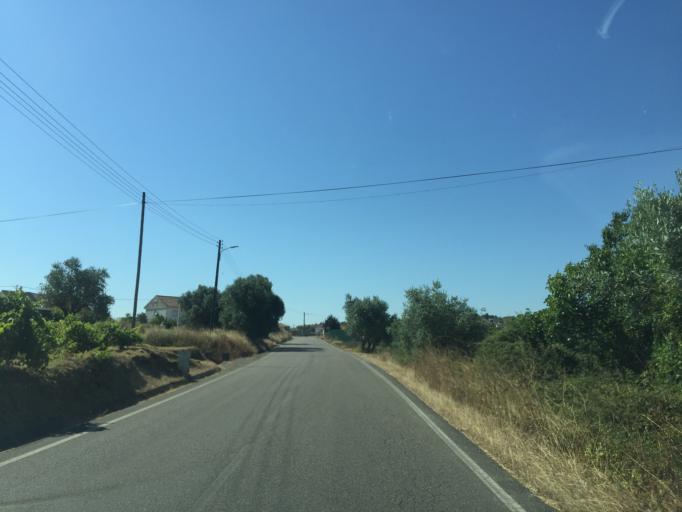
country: PT
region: Santarem
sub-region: Tomar
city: Tomar
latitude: 39.5875
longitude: -8.3278
